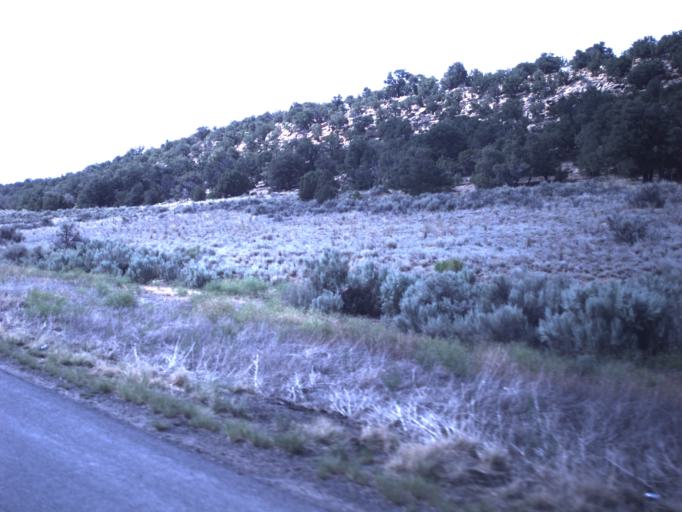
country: US
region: Utah
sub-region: Duchesne County
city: Duchesne
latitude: 40.1804
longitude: -110.6173
